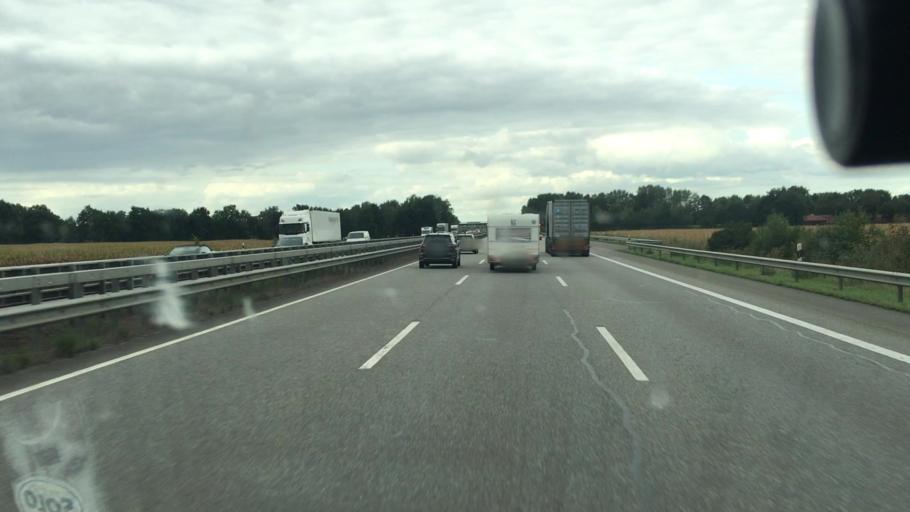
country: DE
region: Lower Saxony
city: Dinklage
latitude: 52.6842
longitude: 8.1727
